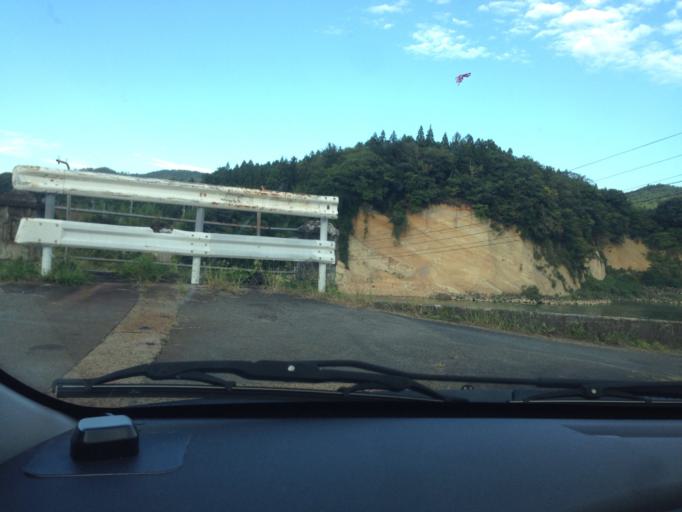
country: JP
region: Fukushima
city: Kitakata
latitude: 37.5747
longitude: 139.7671
